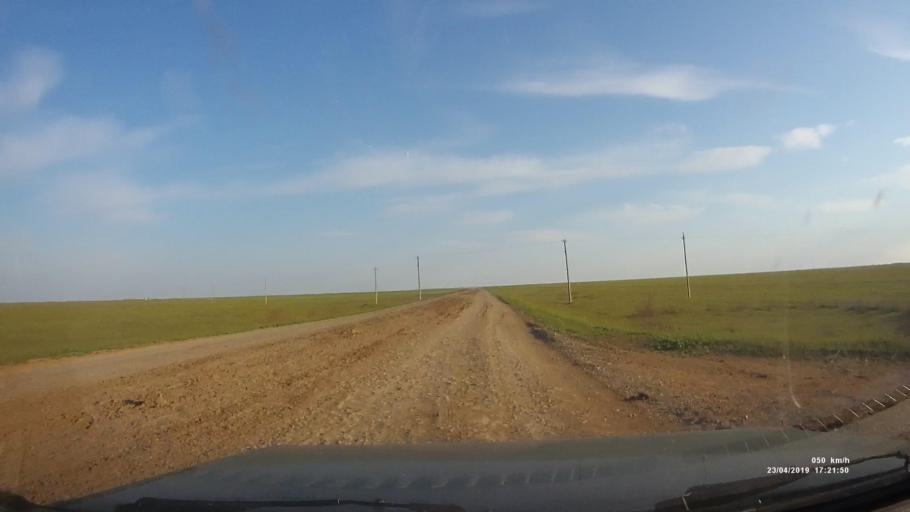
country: RU
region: Kalmykiya
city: Priyutnoye
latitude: 46.1730
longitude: 43.5058
